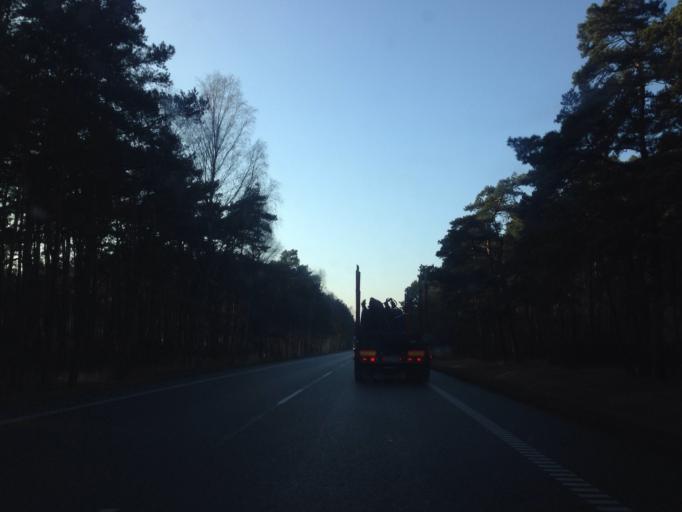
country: PL
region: Kujawsko-Pomorskie
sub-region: Powiat torunski
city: Zlawies Wielka
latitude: 53.0589
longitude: 18.2838
